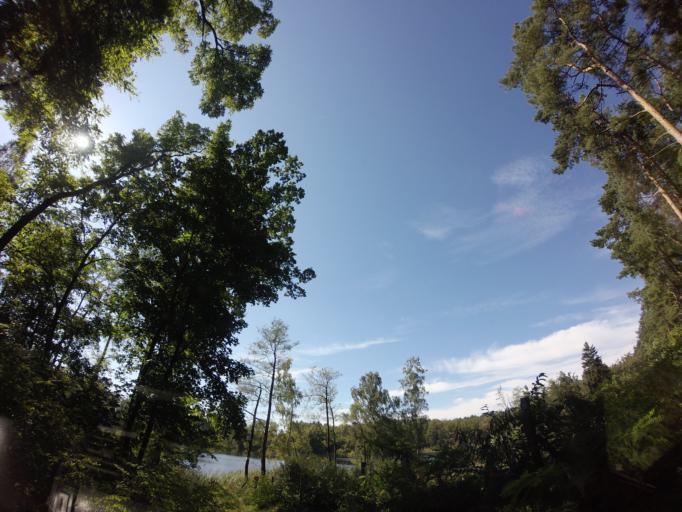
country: PL
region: West Pomeranian Voivodeship
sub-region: Powiat choszczenski
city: Choszczno
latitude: 53.1895
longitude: 15.4985
